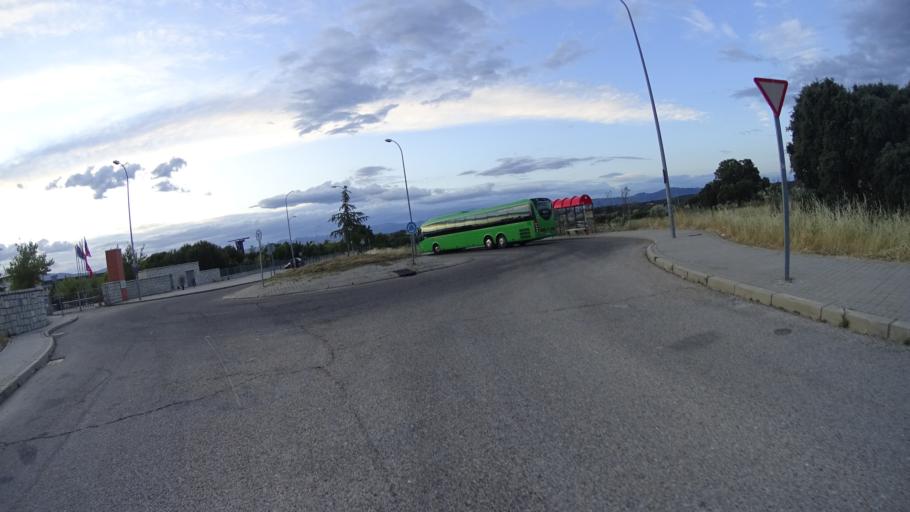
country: ES
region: Madrid
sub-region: Provincia de Madrid
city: Colmenarejo
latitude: 40.5423
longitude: -4.0109
